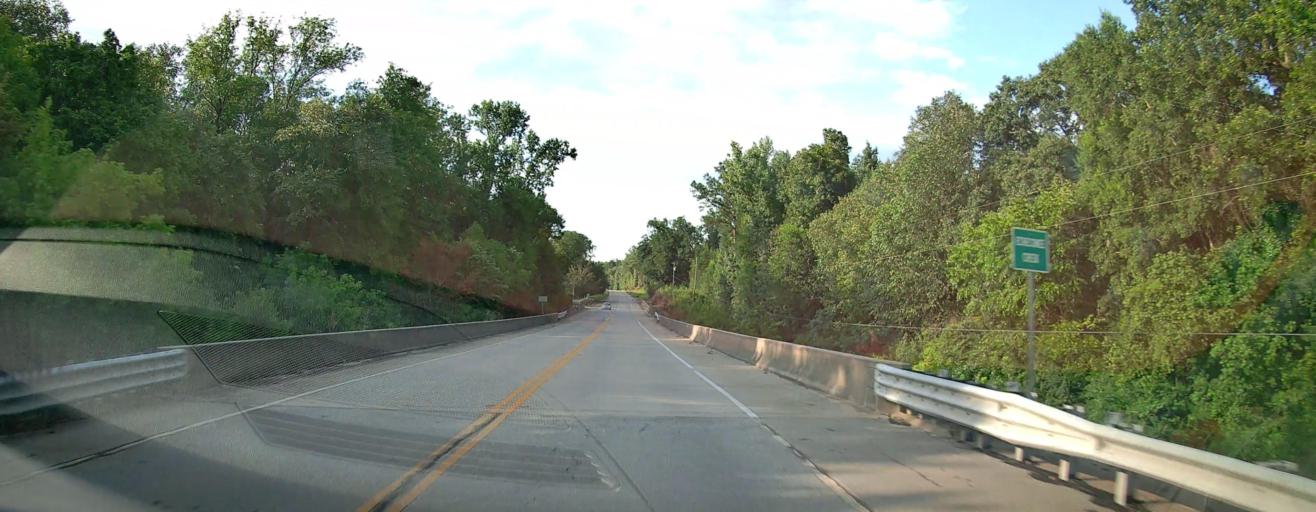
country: US
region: Georgia
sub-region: Crawford County
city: Knoxville
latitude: 32.8653
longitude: -83.9947
